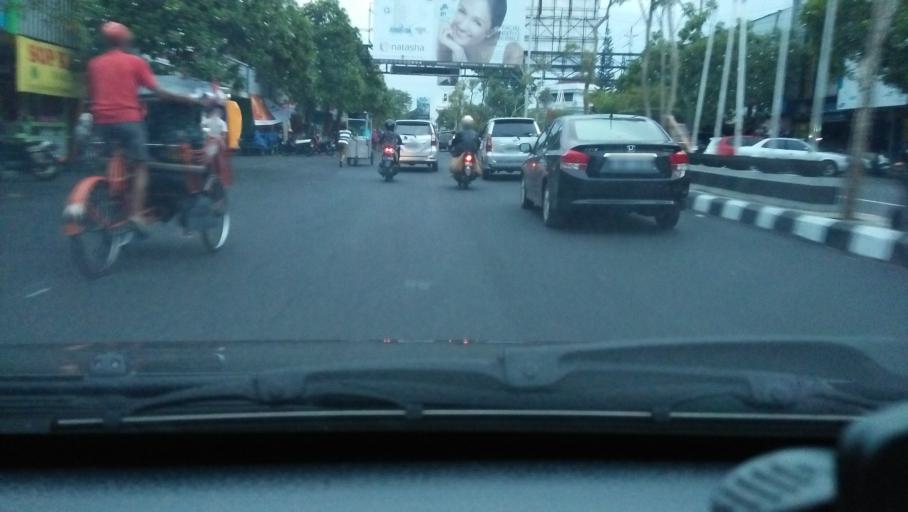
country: ID
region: Central Java
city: Magelang
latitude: -7.4856
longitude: 110.2210
